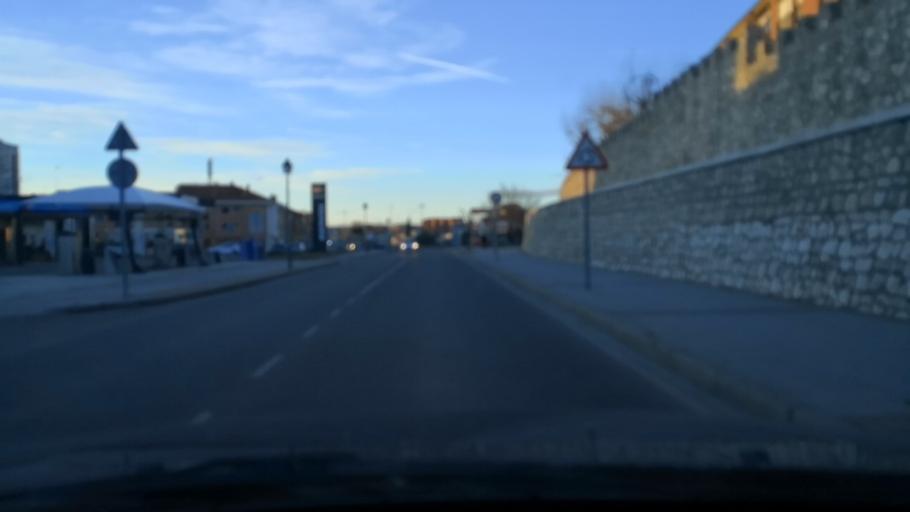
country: ES
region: Castille and Leon
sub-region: Provincia de Valladolid
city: Tordesillas
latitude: 41.5006
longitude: -5.0036
